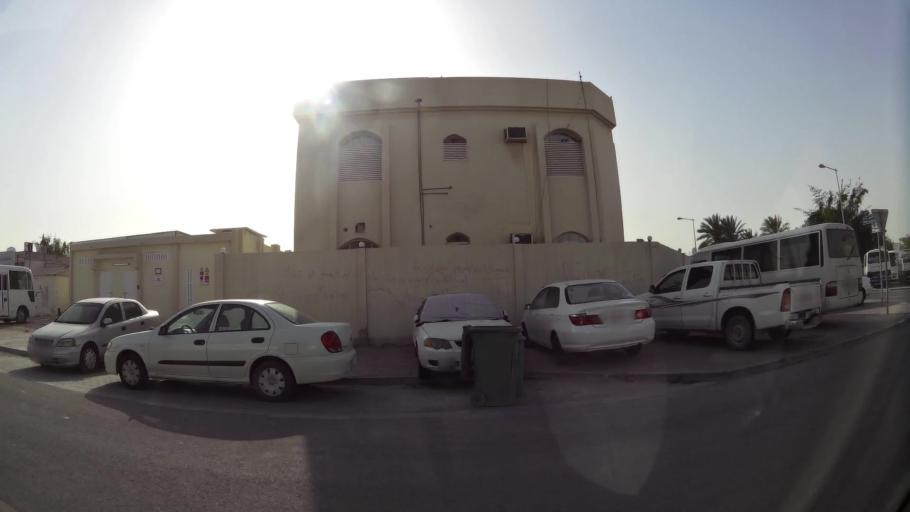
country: QA
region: Baladiyat ar Rayyan
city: Ar Rayyan
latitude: 25.2381
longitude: 51.4344
